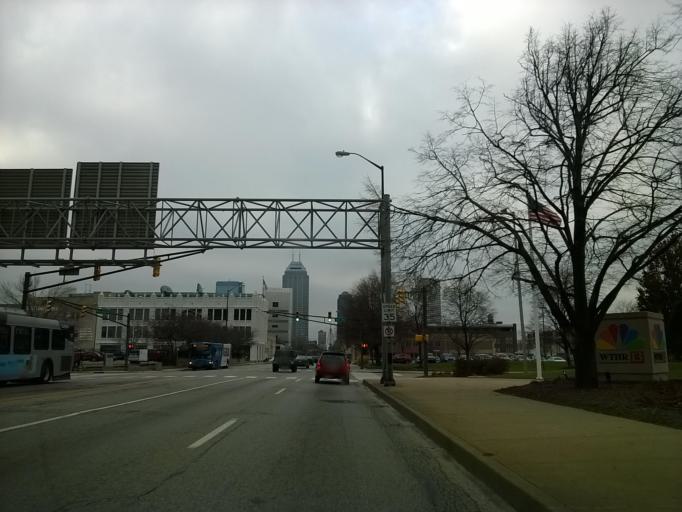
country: US
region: Indiana
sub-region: Marion County
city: Indianapolis
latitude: 39.7816
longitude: -86.1576
